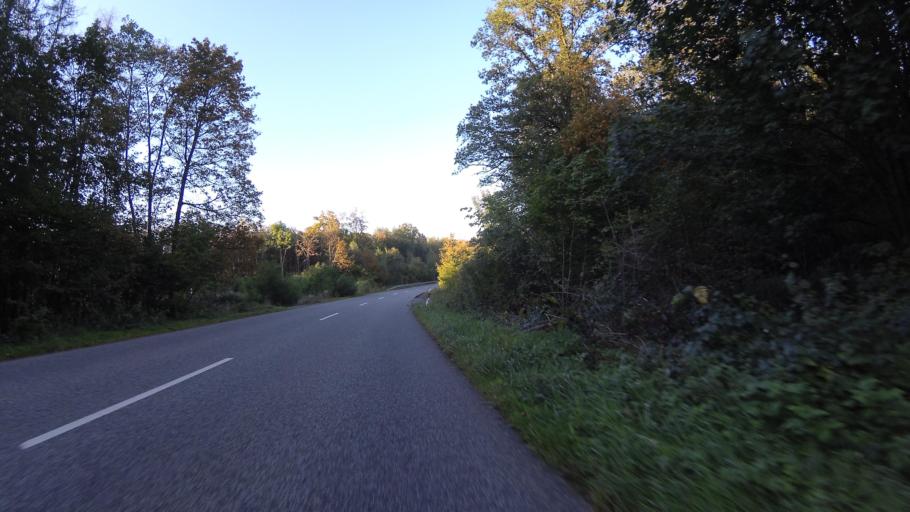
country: DE
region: Saarland
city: Friedrichsthal
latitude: 49.3381
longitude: 7.1128
